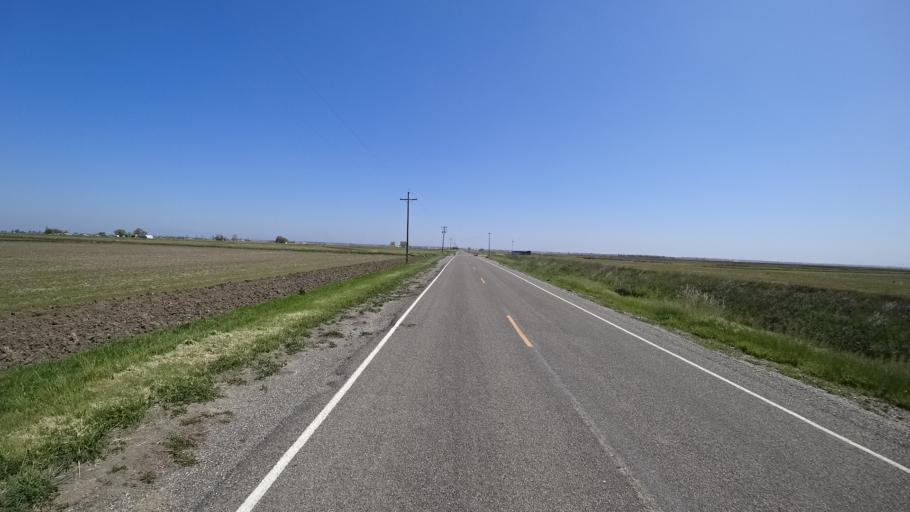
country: US
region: California
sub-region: Glenn County
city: Willows
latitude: 39.5582
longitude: -122.0738
